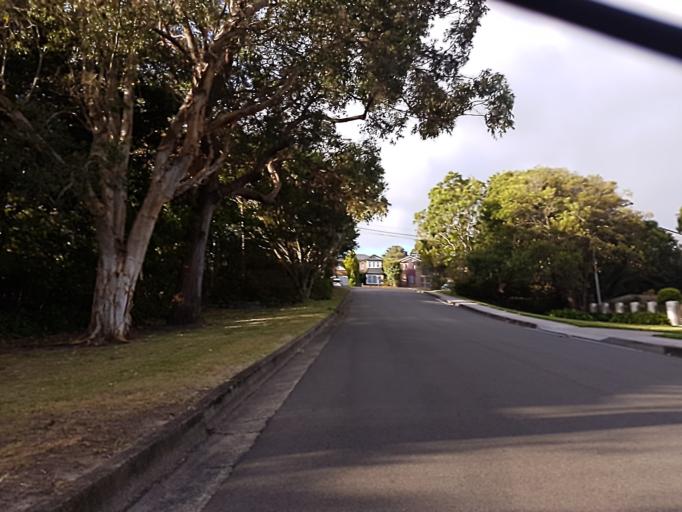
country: AU
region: New South Wales
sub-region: Manly Vale
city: Balgowlah
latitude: -33.7959
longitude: 151.2417
